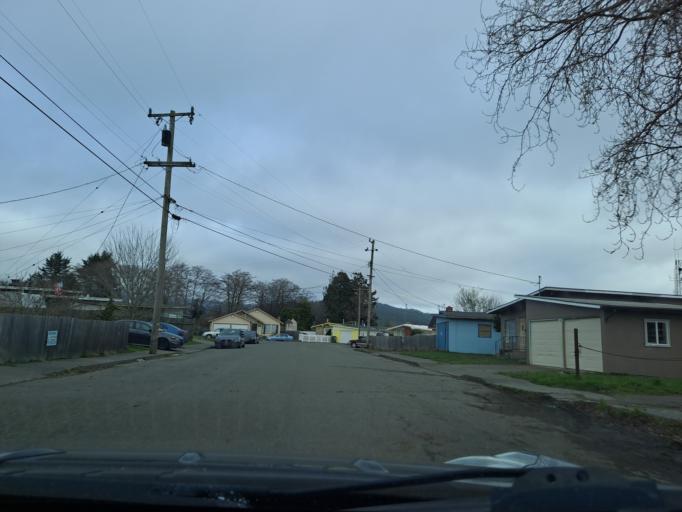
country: US
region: California
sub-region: Humboldt County
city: Fortuna
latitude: 40.5930
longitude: -124.1490
